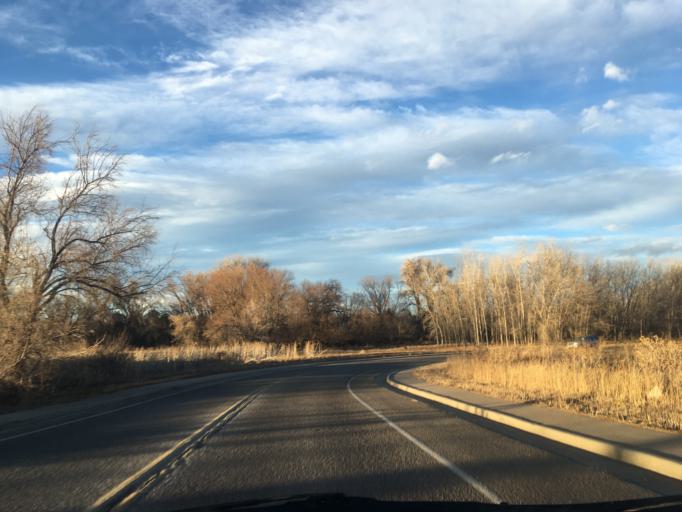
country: US
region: Colorado
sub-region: Jefferson County
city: Applewood
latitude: 39.8205
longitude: -105.1586
